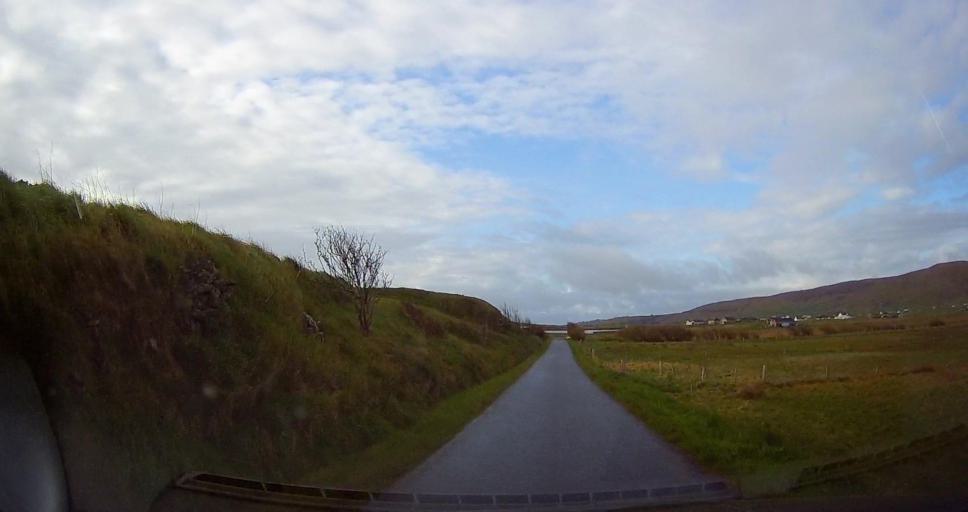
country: GB
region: Scotland
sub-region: Shetland Islands
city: Sandwick
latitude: 60.0497
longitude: -1.2065
